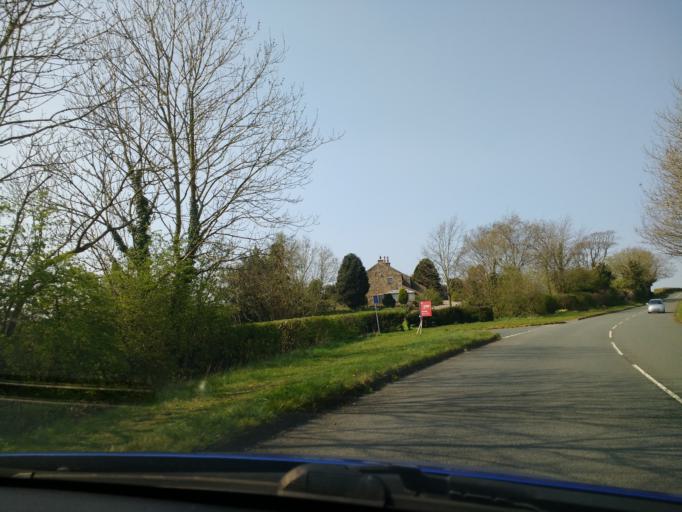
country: GB
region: England
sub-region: Lancashire
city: Bolton le Sands
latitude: 54.0828
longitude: -2.7853
